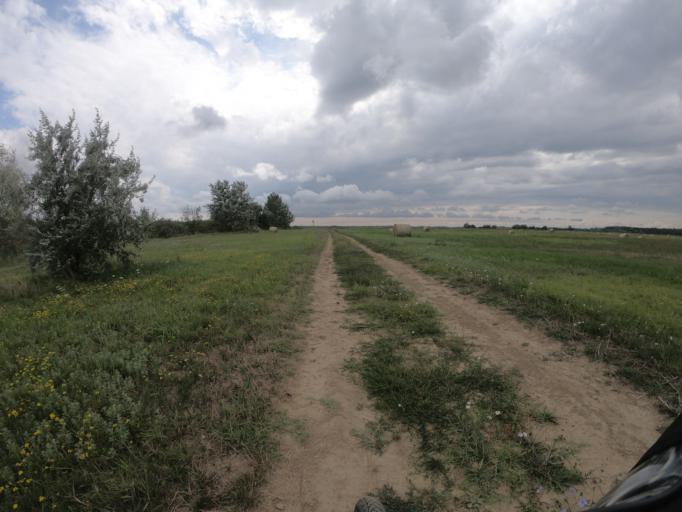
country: HU
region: Jasz-Nagykun-Szolnok
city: Tiszafured
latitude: 47.7098
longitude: 20.7787
